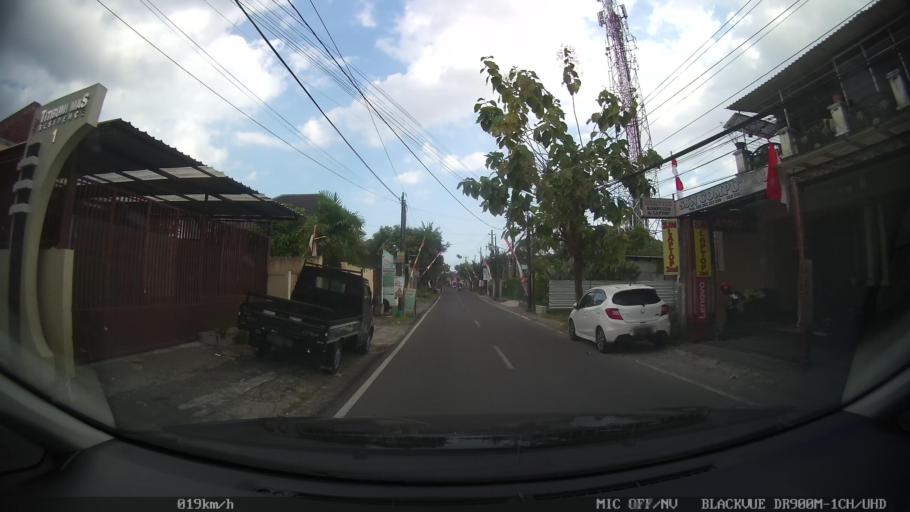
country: ID
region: Daerah Istimewa Yogyakarta
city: Yogyakarta
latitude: -7.7799
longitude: 110.3408
